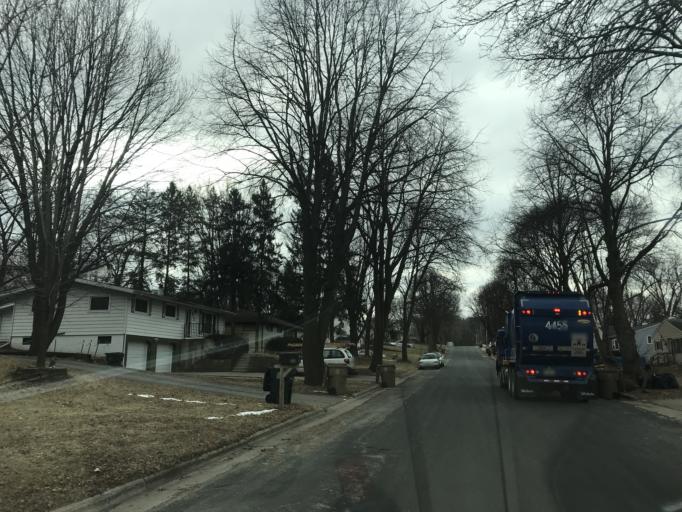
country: US
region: Wisconsin
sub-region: Dane County
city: Monona
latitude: 43.1101
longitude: -89.3059
